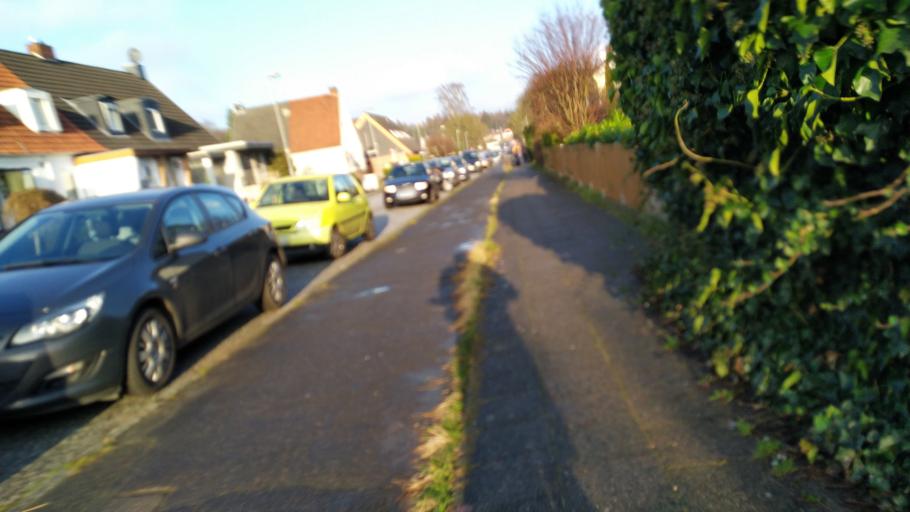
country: DE
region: Mecklenburg-Vorpommern
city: Selmsdorf
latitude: 53.9195
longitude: 10.8145
